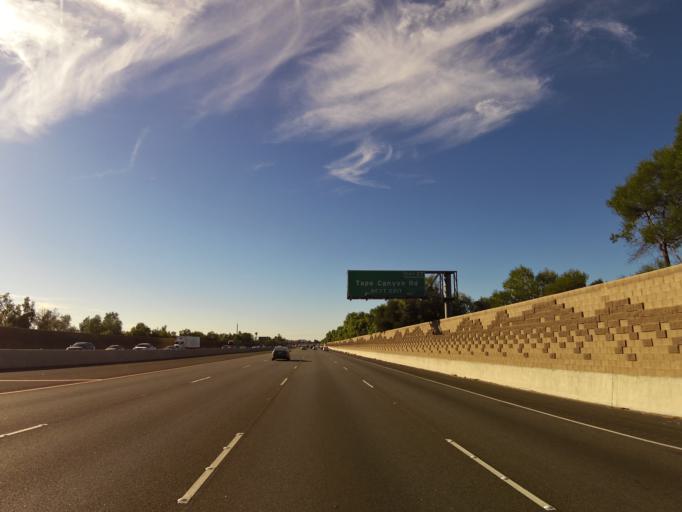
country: US
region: California
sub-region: Ventura County
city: Santa Susana
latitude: 34.2819
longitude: -118.7044
